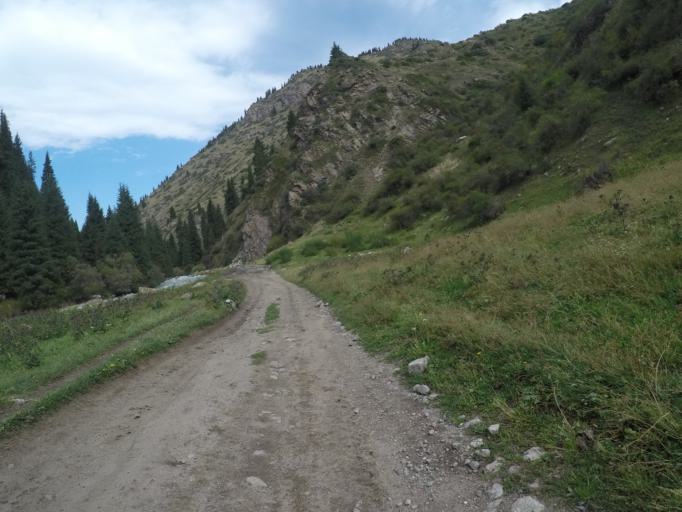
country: KG
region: Ysyk-Koel
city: Teploklyuchenka
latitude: 42.4396
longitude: 78.5578
